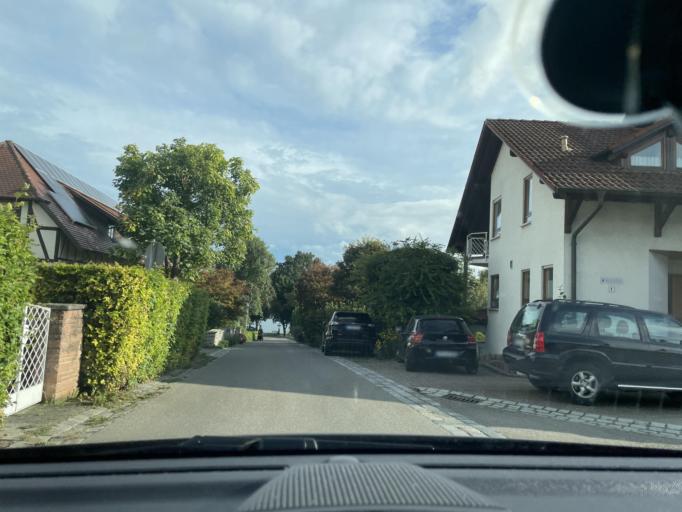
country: DE
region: Baden-Wuerttemberg
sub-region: Tuebingen Region
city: Immenstaad am Bodensee
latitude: 47.6630
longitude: 9.3581
